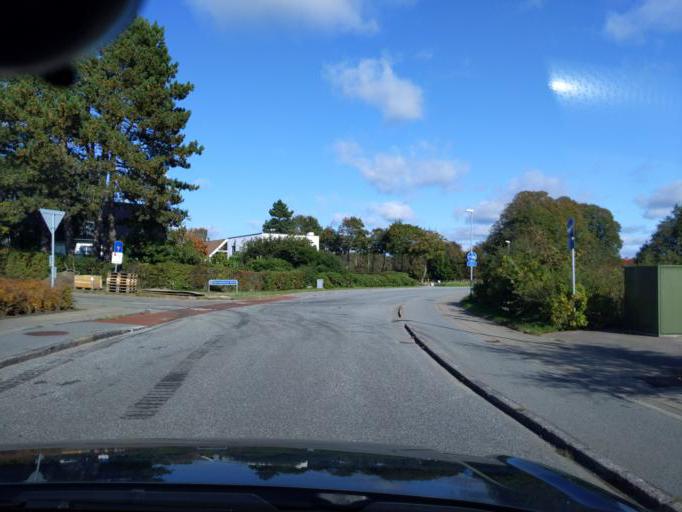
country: DK
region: Central Jutland
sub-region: Viborg Kommune
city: Viborg
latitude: 56.4683
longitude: 9.4258
